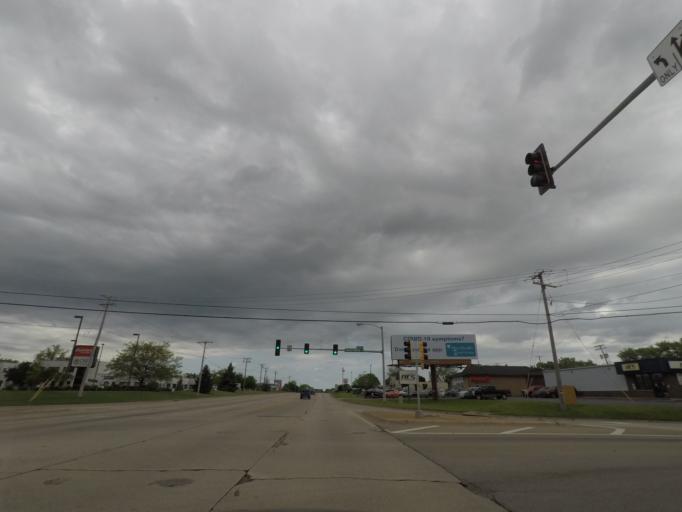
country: US
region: Illinois
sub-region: Winnebago County
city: Cherry Valley
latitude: 42.2238
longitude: -89.0287
